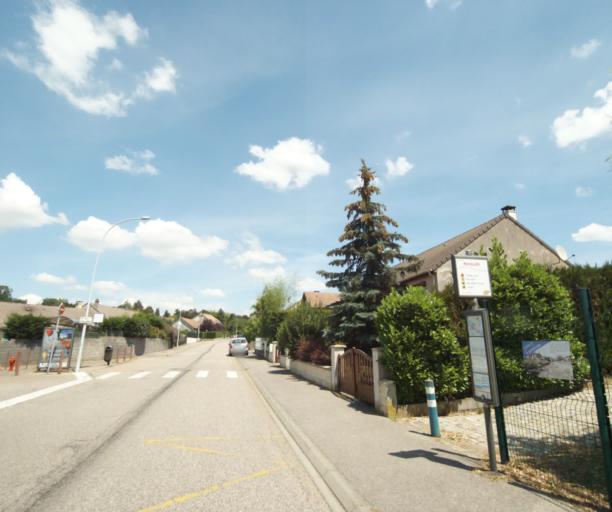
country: FR
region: Lorraine
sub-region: Departement de Meurthe-et-Moselle
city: Luneville
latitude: 48.6036
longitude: 6.4806
